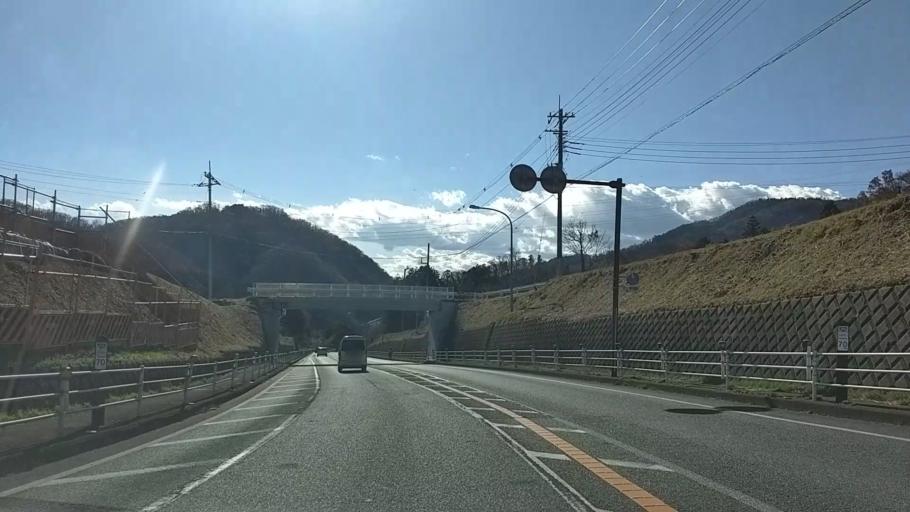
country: JP
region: Kanagawa
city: Hadano
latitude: 35.3737
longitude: 139.1636
